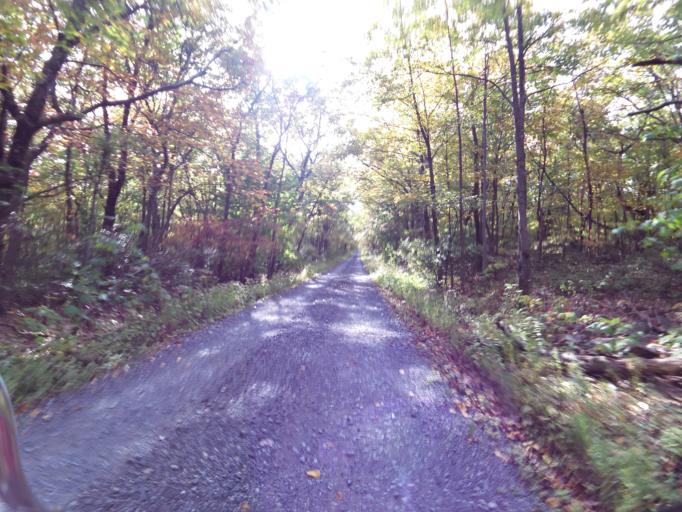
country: US
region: Pennsylvania
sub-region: Lycoming County
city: Jersey Shore
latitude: 41.1074
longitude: -77.1587
